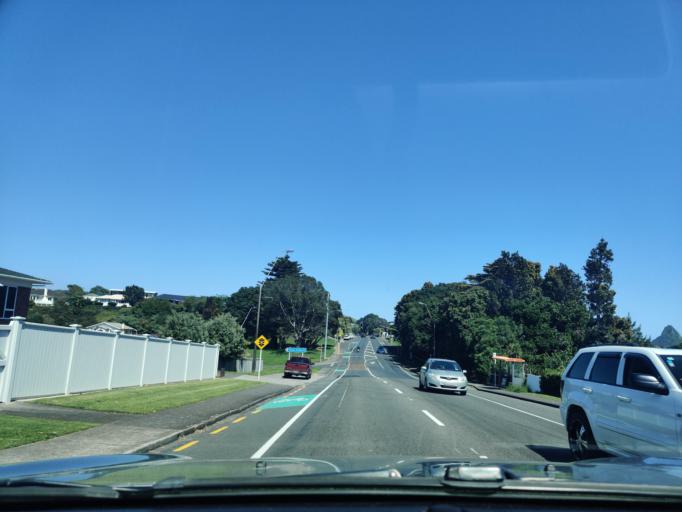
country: NZ
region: Taranaki
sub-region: New Plymouth District
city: New Plymouth
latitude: -39.0636
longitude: 174.0551
